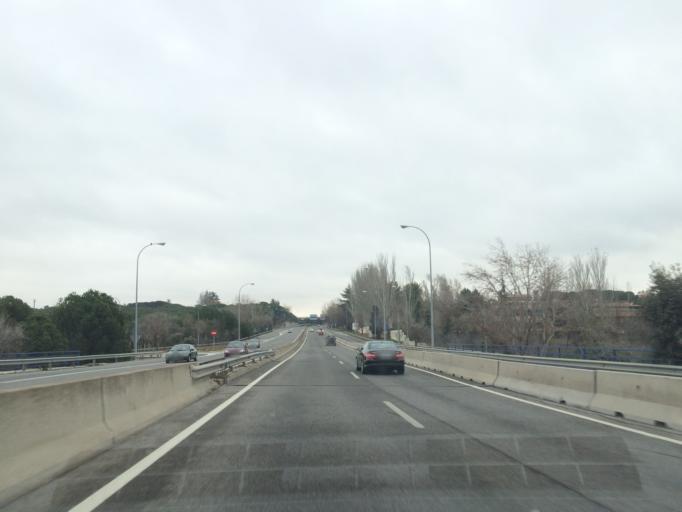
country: ES
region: Madrid
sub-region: Provincia de Madrid
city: Moncloa-Aravaca
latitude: 40.4543
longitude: -3.7663
